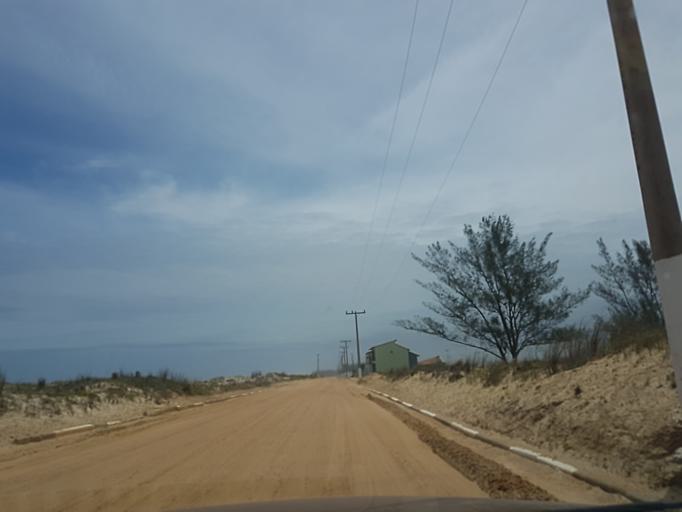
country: BR
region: Santa Catarina
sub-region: Jaguaruna
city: Jaguaruna
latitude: -28.6647
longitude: -48.9633
